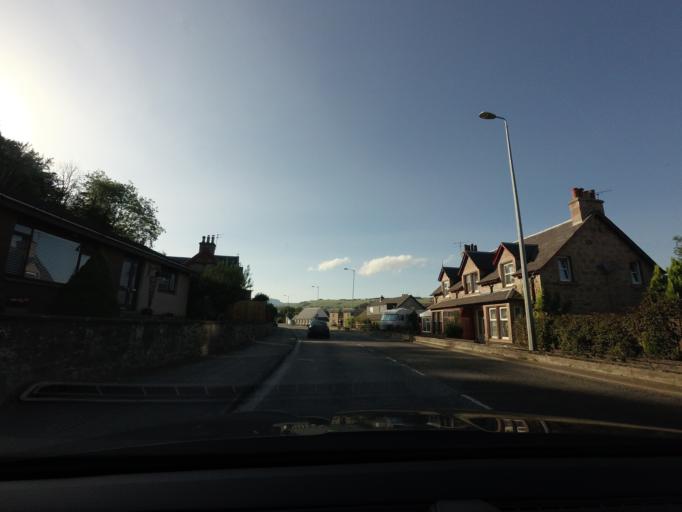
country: GB
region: Scotland
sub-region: Highland
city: Dingwall
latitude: 57.5928
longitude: -4.4243
